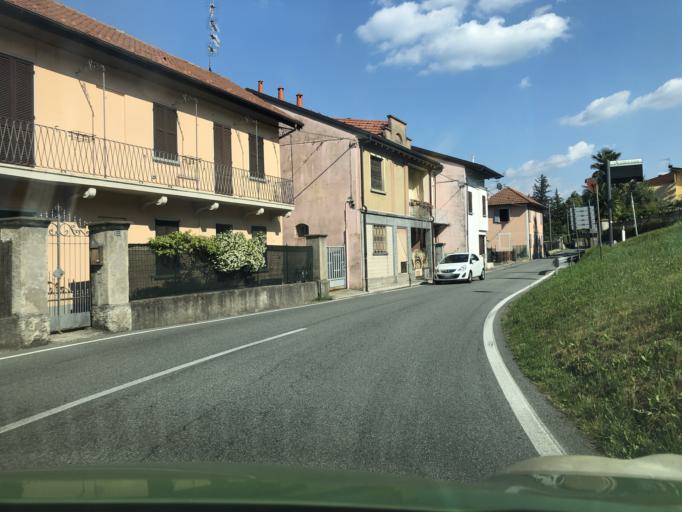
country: IT
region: Piedmont
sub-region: Provincia di Novara
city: Meina
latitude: 45.7738
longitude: 8.5399
